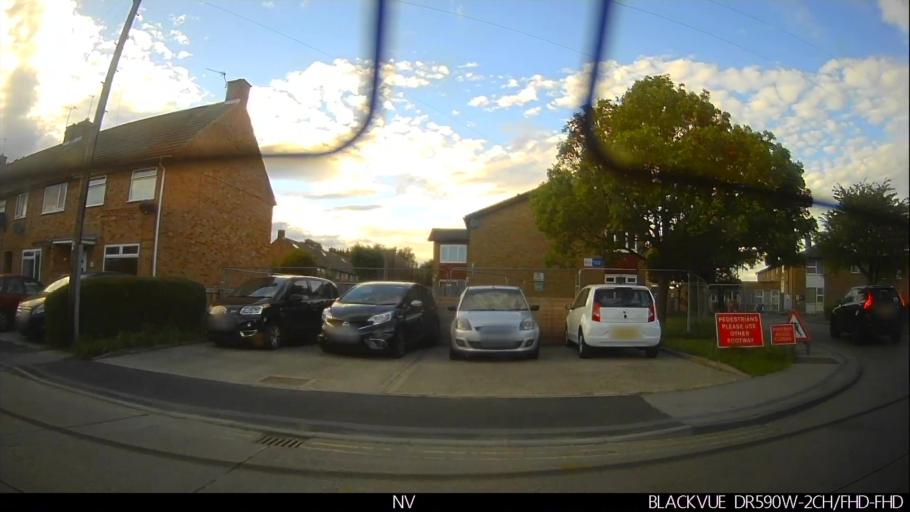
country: GB
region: England
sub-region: City of York
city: Bishopthorpe
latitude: 53.9479
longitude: -1.1210
